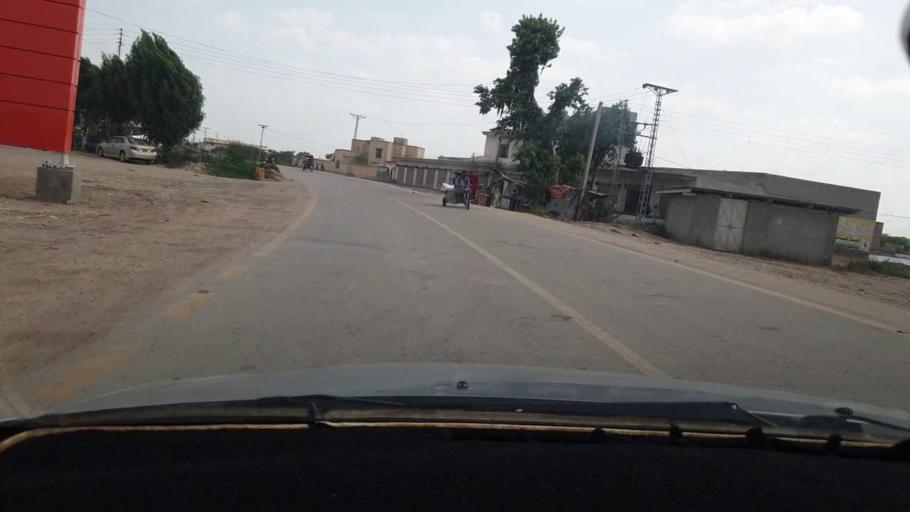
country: PK
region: Sindh
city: Digri
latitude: 25.0599
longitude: 69.2179
